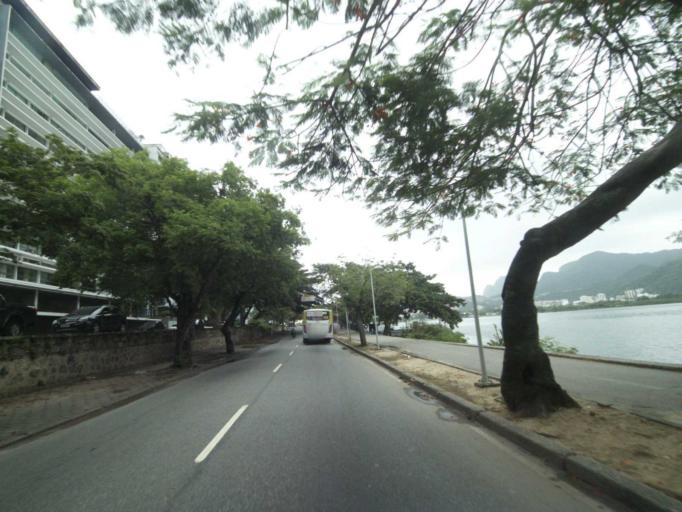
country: BR
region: Rio de Janeiro
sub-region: Rio De Janeiro
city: Rio de Janeiro
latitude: -22.9707
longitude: -43.2070
